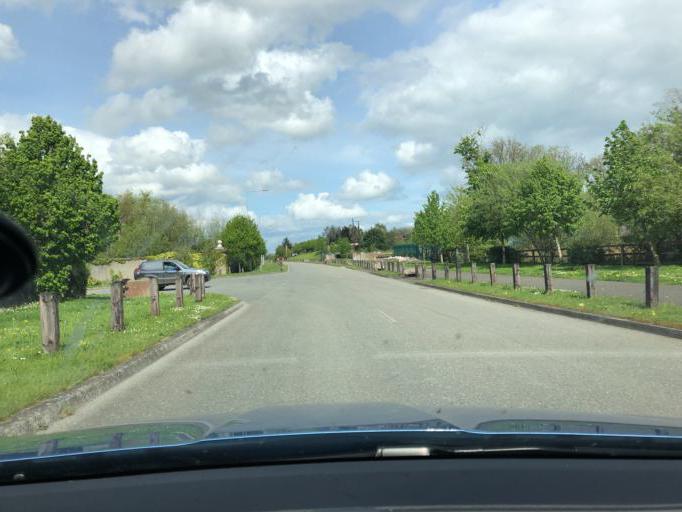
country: IE
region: Leinster
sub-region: Kildare
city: Johnstown
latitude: 53.2438
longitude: -6.6103
